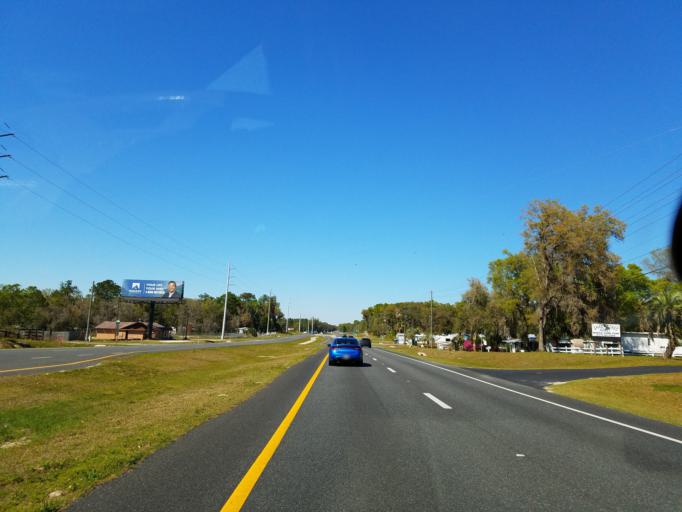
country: US
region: Florida
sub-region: Marion County
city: Belleview
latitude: 28.9754
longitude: -82.0412
